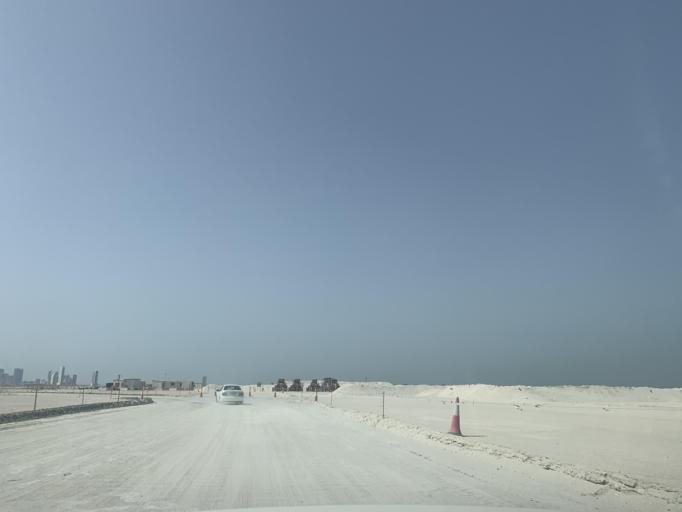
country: BH
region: Northern
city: Sitrah
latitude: 26.1671
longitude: 50.6362
